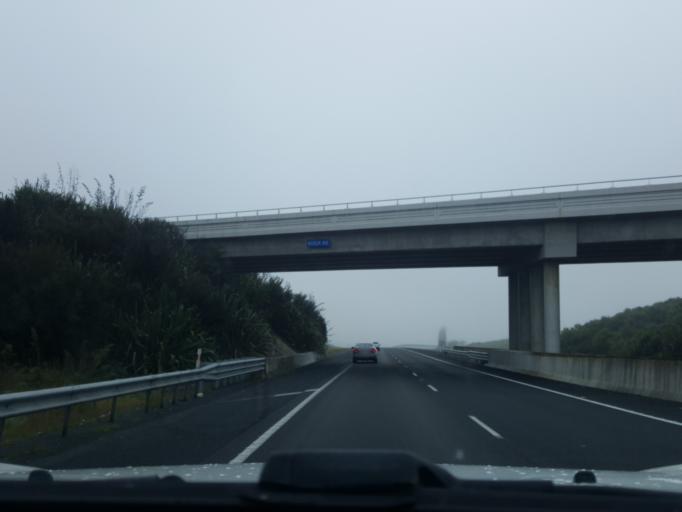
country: NZ
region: Waikato
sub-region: Waikato District
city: Ngaruawahia
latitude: -37.6975
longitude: 175.2115
